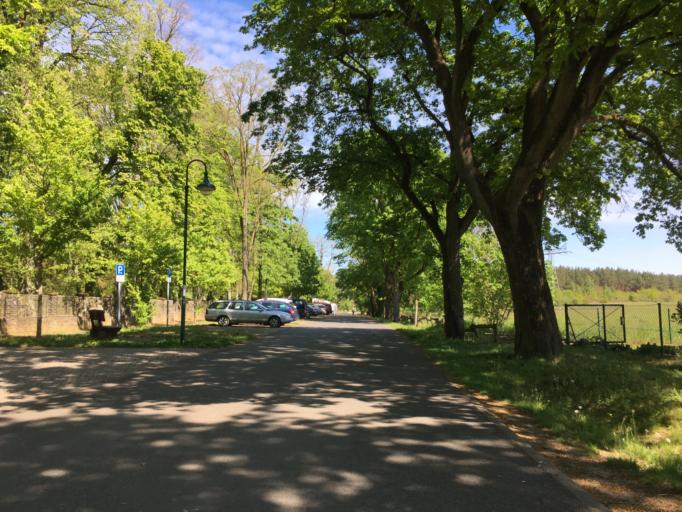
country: DE
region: Brandenburg
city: Bernau bei Berlin
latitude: 52.6819
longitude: 13.5324
